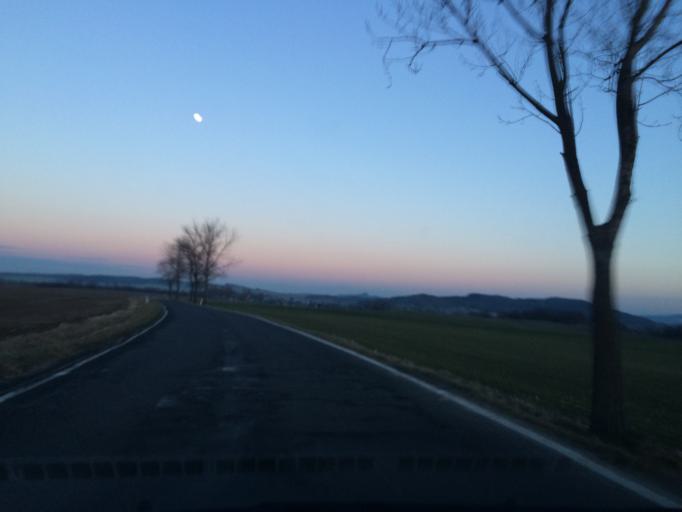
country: PL
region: Lower Silesian Voivodeship
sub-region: Powiat zlotoryjski
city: Olszanica
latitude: 51.1196
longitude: 15.7855
